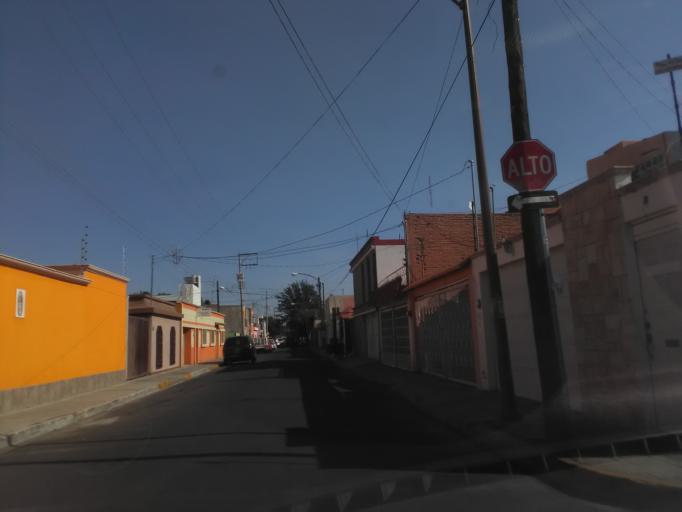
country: MX
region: Durango
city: Victoria de Durango
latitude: 24.0335
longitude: -104.6624
